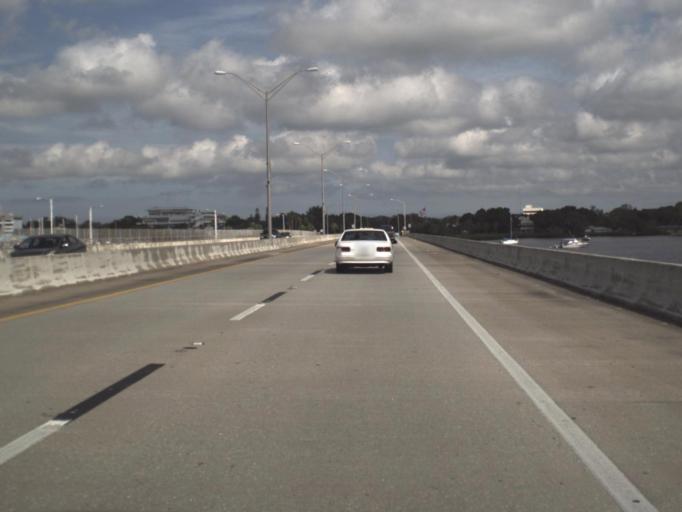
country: US
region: Florida
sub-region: Manatee County
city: Bradenton
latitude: 27.5070
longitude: -82.5720
